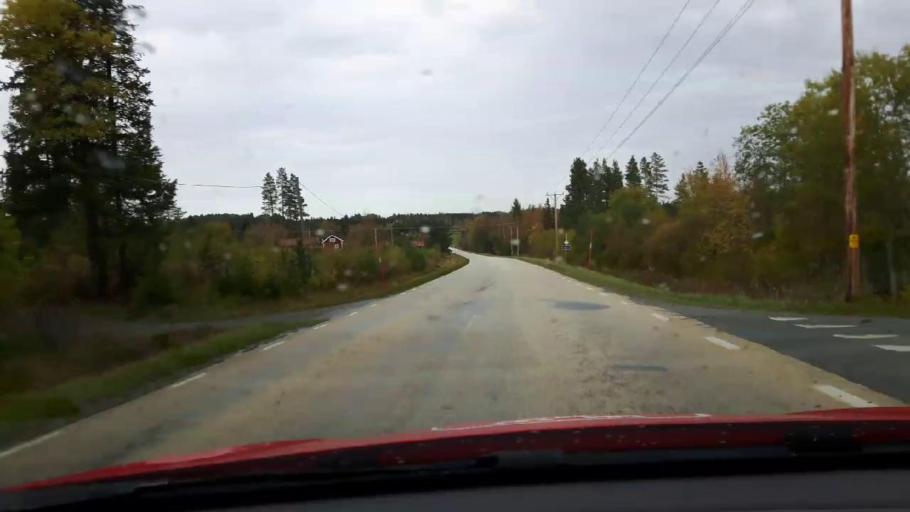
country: SE
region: Jaemtland
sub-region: Bergs Kommun
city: Hoverberg
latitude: 62.9723
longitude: 14.3489
